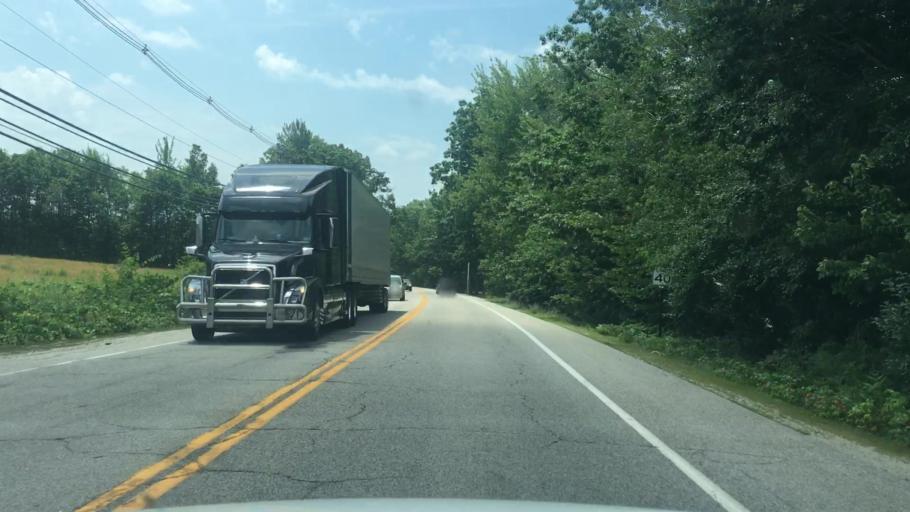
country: US
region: Maine
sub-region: York County
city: Sanford (historical)
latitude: 43.4585
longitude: -70.7625
